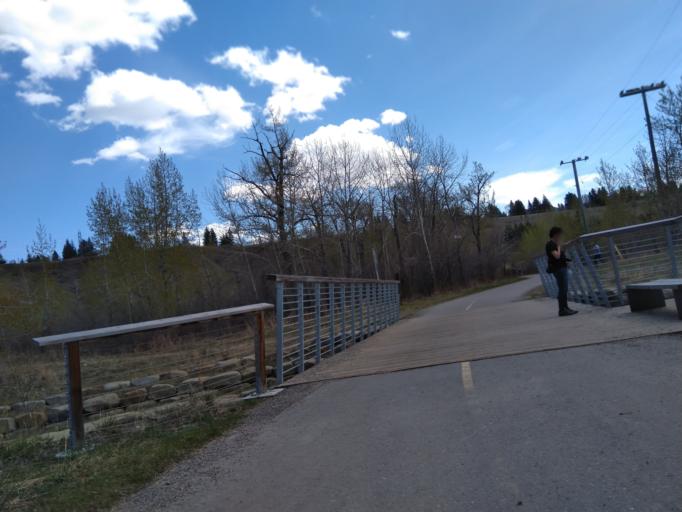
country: CA
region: Alberta
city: Calgary
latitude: 51.0857
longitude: -114.1689
